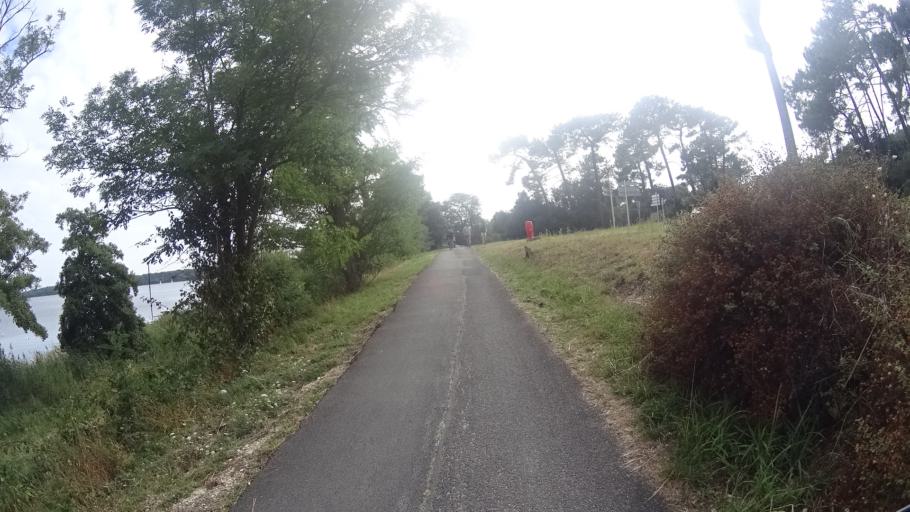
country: FR
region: Aquitaine
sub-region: Departement de la Gironde
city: Lacanau
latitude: 45.0002
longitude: -1.1387
